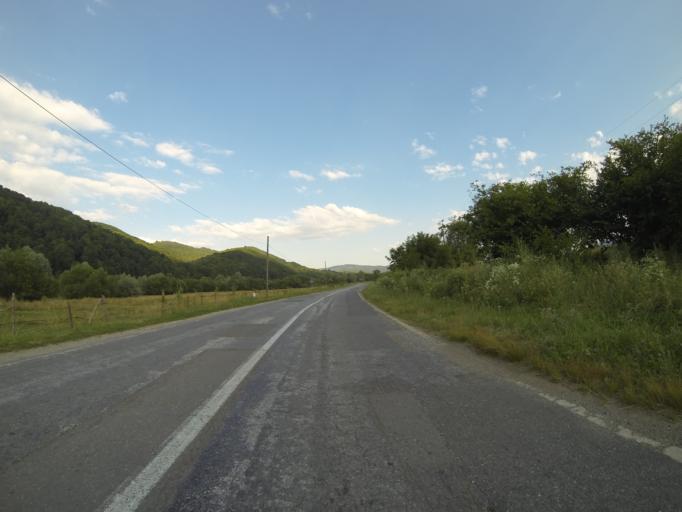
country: RO
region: Brasov
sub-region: Comuna Sinca Noua
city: Sinca Noua
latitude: 45.7375
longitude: 25.2278
